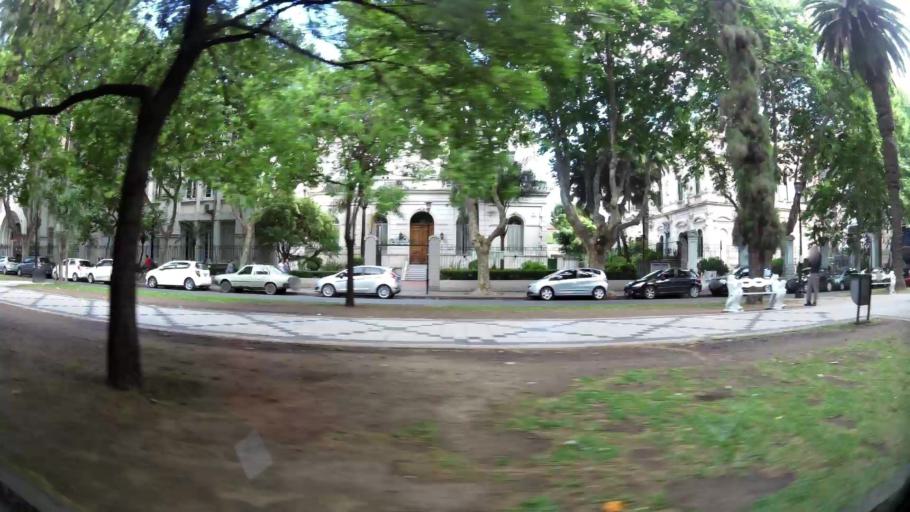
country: AR
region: Santa Fe
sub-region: Departamento de Rosario
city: Rosario
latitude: -32.9458
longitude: -60.6539
